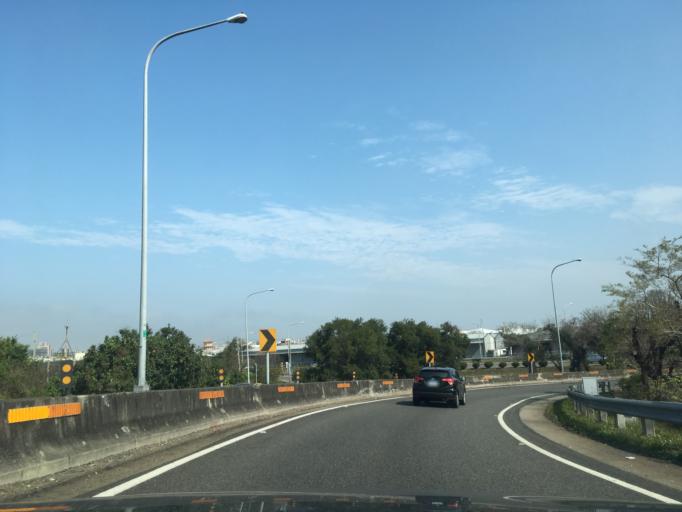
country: TW
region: Taiwan
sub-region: Taichung City
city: Taichung
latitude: 24.2060
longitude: 120.6549
